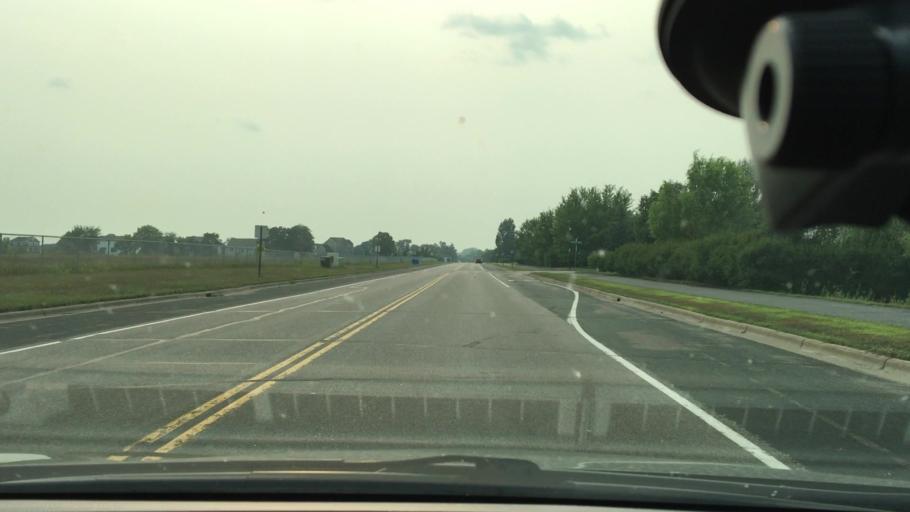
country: US
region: Minnesota
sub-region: Wright County
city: Otsego
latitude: 45.2633
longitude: -93.5631
